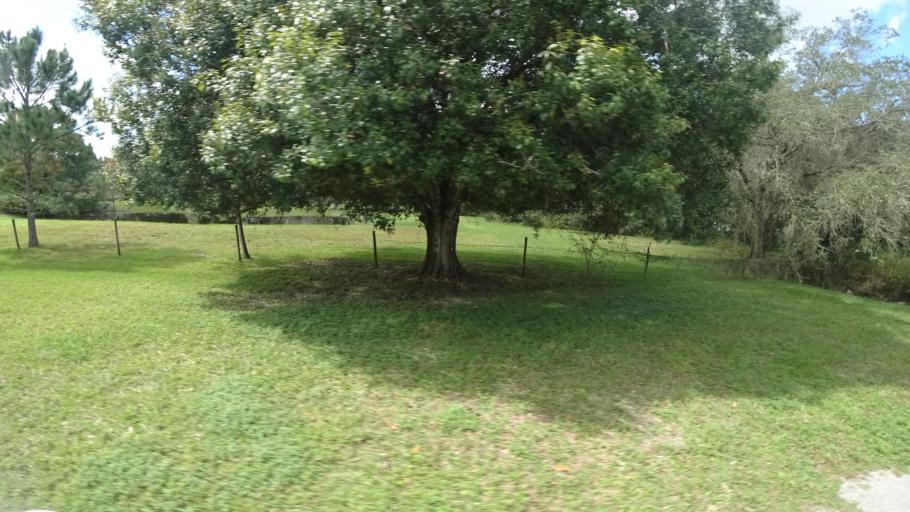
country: US
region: Florida
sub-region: Sarasota County
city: Lake Sarasota
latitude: 27.2866
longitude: -82.2303
